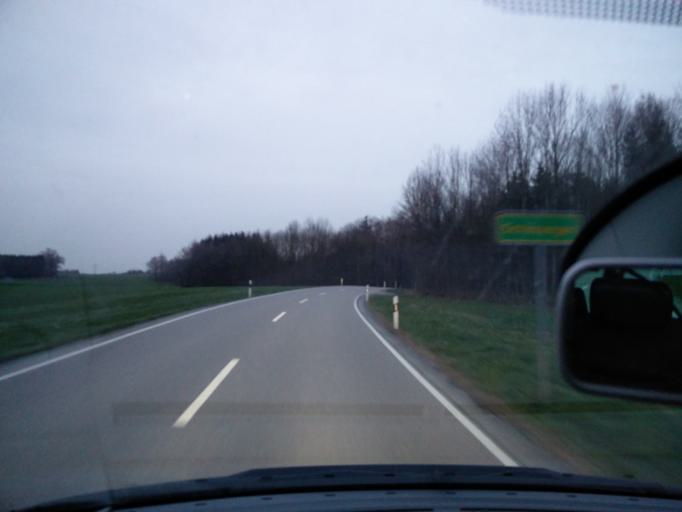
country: DE
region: Bavaria
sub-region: Upper Bavaria
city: Albaching
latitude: 48.1208
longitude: 12.0894
